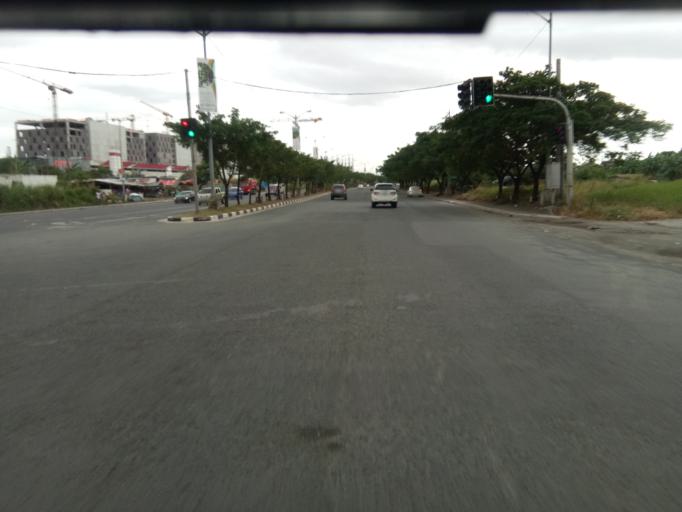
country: PH
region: Metro Manila
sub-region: Makati City
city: Makati City
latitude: 14.5151
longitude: 120.9900
